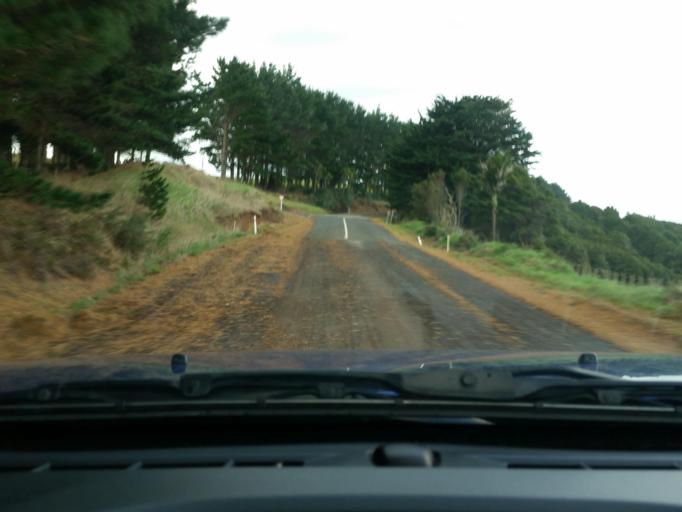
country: NZ
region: Northland
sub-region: Kaipara District
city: Dargaville
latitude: -35.7572
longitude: 173.6143
